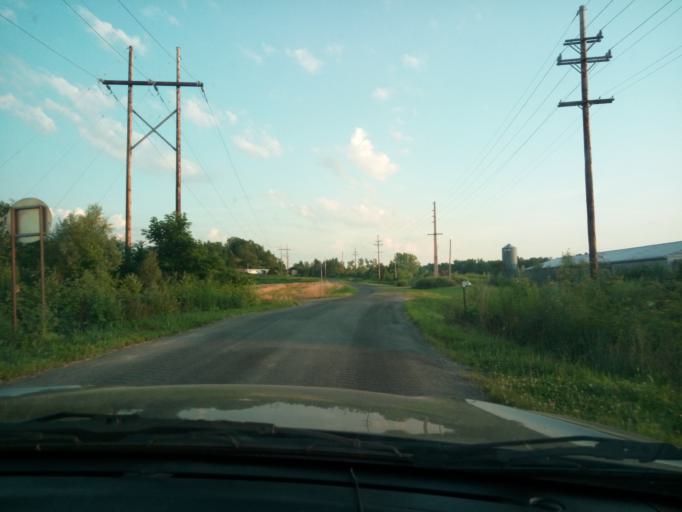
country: US
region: New York
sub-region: Wayne County
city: Clyde
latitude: 43.0635
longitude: -76.8328
